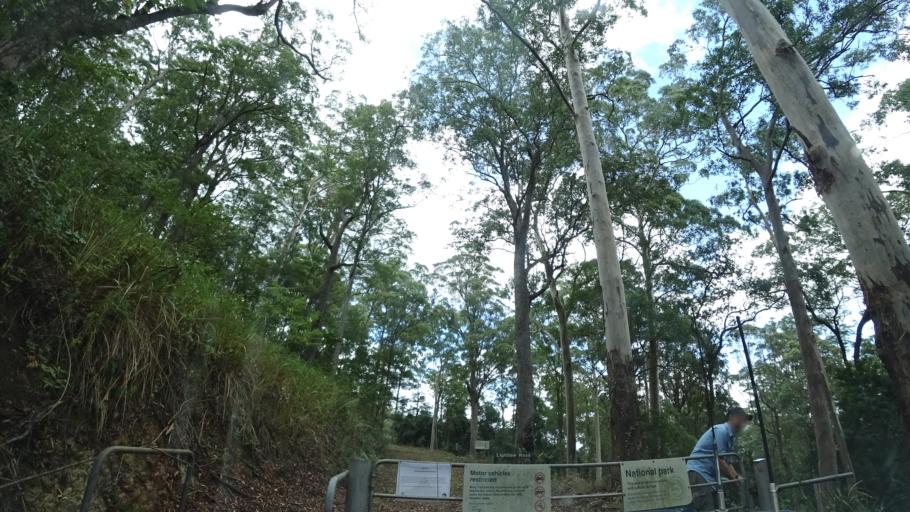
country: AU
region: Queensland
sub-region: Moreton Bay
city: Highvale
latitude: -27.4017
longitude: 152.7754
